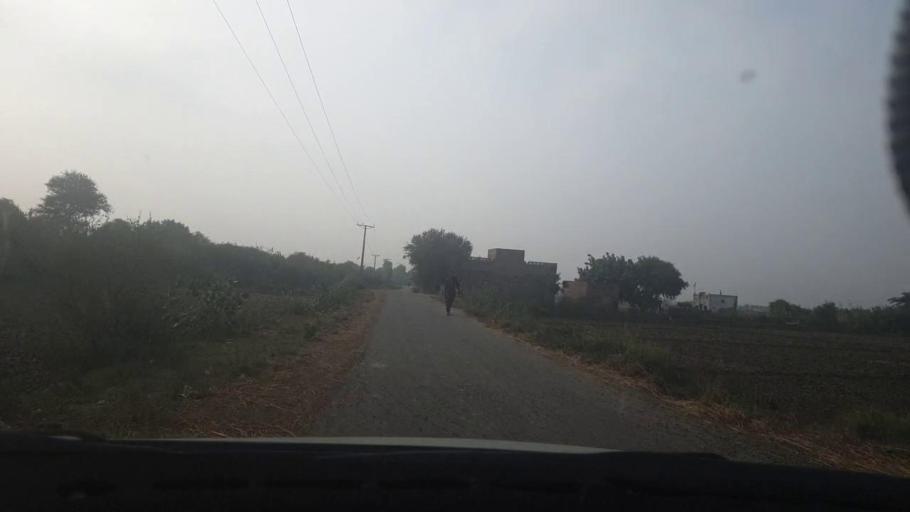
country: PK
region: Sindh
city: Tando Muhammad Khan
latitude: 25.0921
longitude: 68.5164
